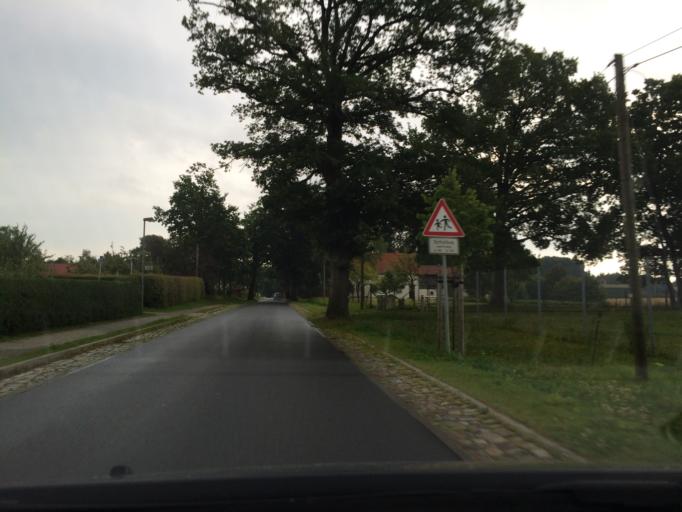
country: DE
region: Mecklenburg-Vorpommern
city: Prohn
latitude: 54.3489
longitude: 13.0155
